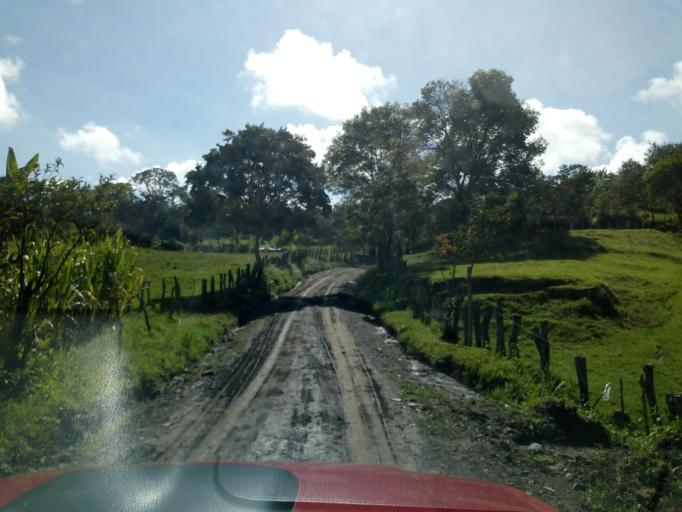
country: CO
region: Boyaca
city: Moniquira
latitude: 5.8900
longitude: -73.5236
